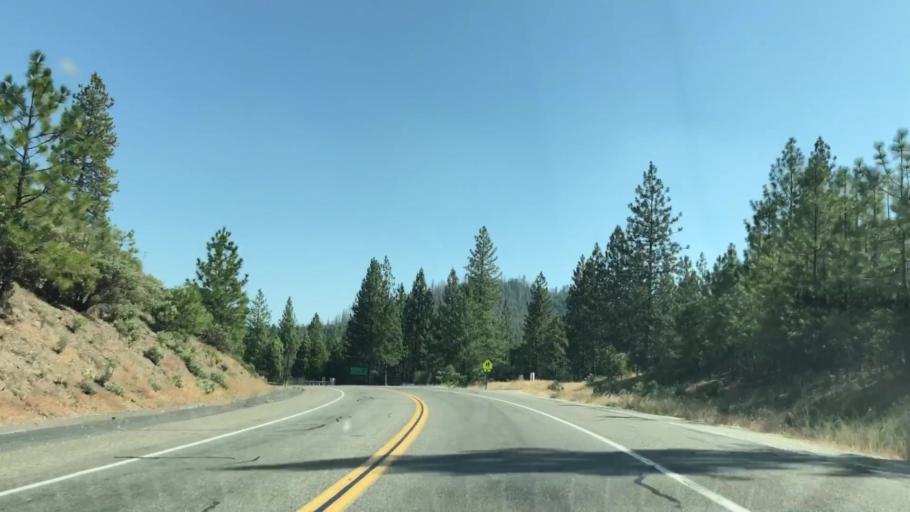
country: US
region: California
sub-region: Tuolumne County
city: Tuolumne City
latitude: 37.8368
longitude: -120.2210
